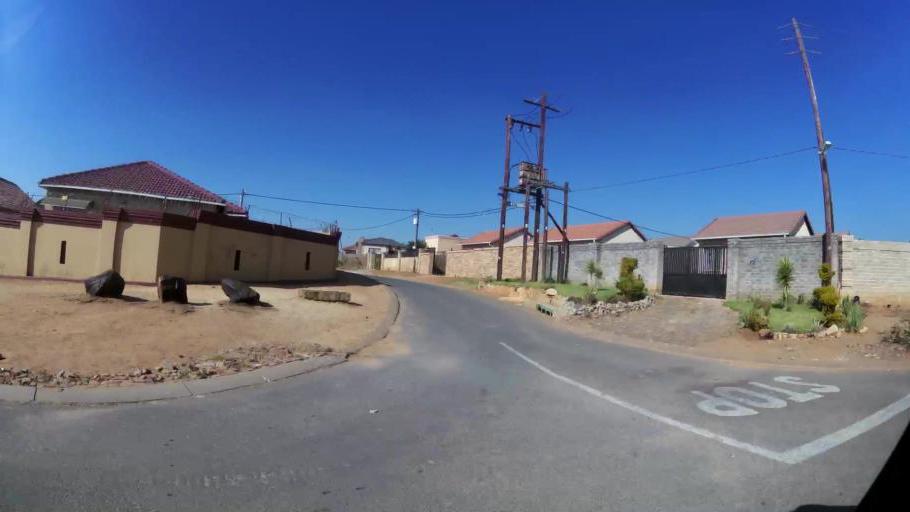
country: ZA
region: Gauteng
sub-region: West Rand District Municipality
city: Muldersdriseloop
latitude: -26.0384
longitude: 27.9268
